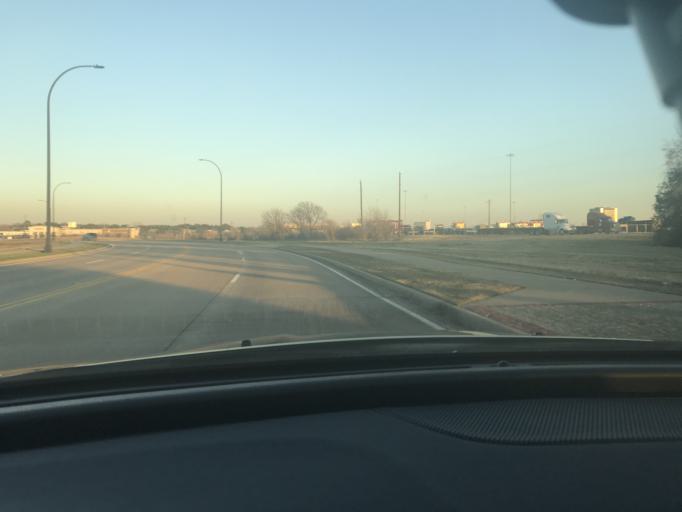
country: US
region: Texas
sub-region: Tarrant County
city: Arlington
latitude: 32.7616
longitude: -97.1014
